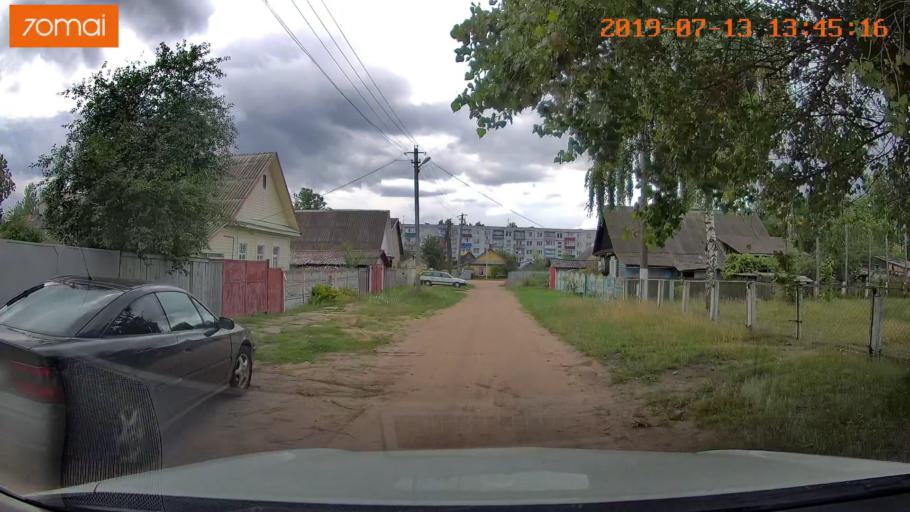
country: BY
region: Mogilev
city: Asipovichy
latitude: 53.2971
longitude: 28.6355
